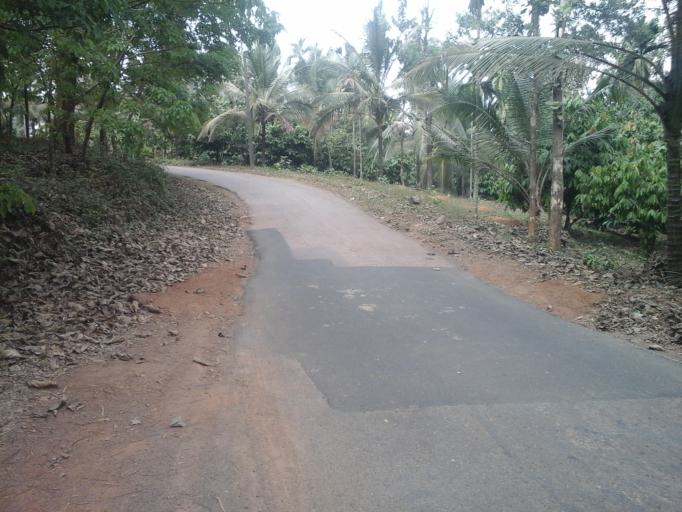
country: IN
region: Kerala
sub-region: Kannur
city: Taliparamba
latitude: 12.1454
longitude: 75.4419
